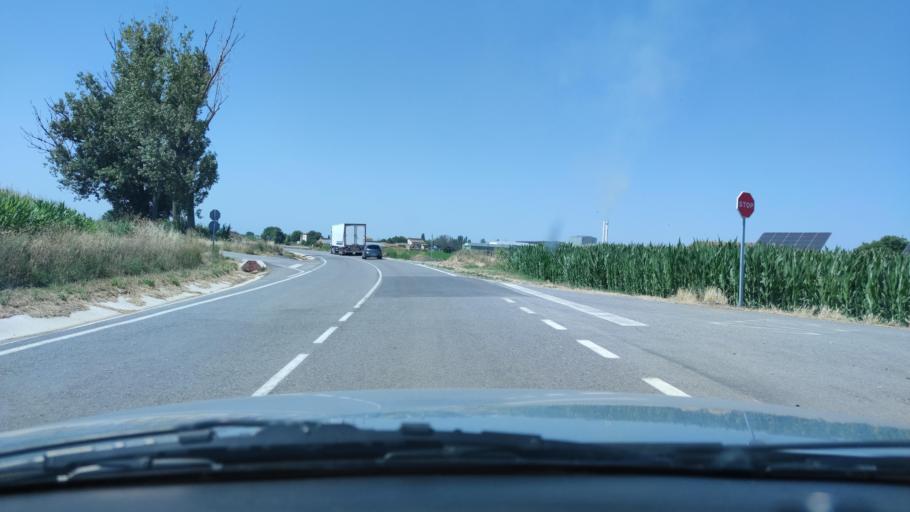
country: ES
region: Catalonia
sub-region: Provincia de Lleida
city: Ivars d'Urgell
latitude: 41.6877
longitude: 0.9844
